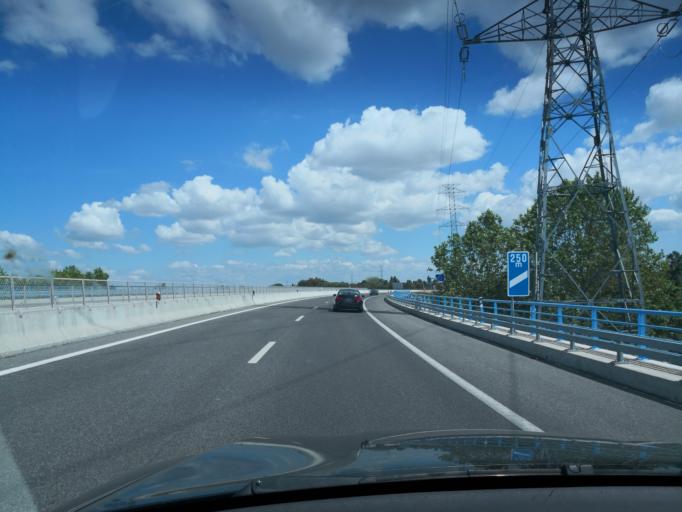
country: PT
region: Setubal
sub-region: Seixal
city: Amora
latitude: 38.6059
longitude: -9.1374
